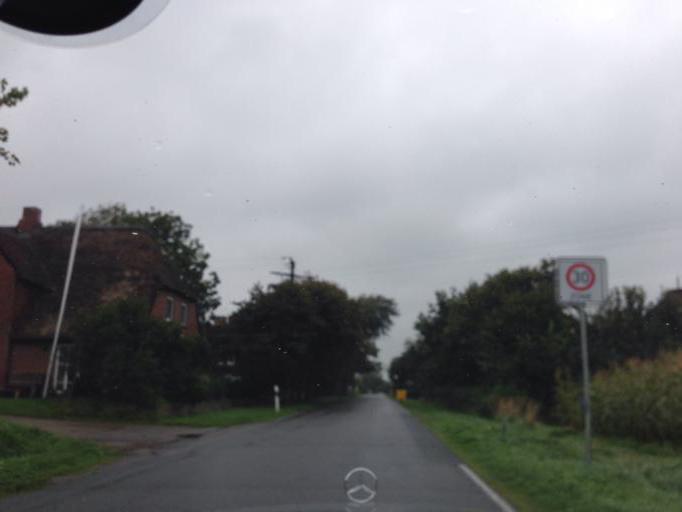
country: DE
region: Schleswig-Holstein
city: Dunsum
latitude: 54.7284
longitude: 8.4136
